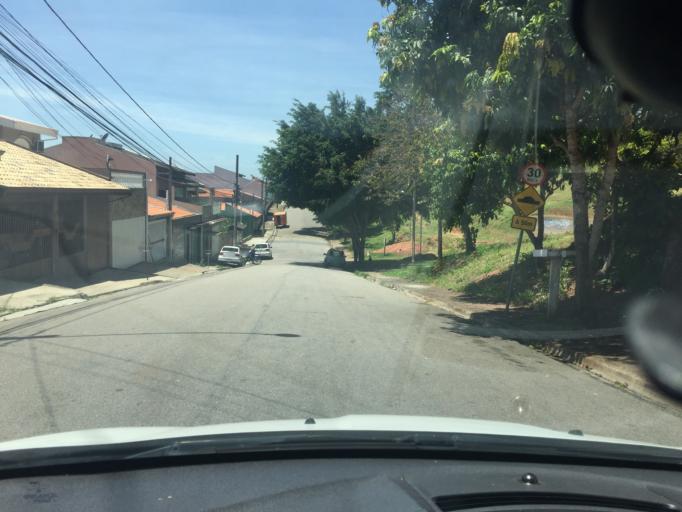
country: BR
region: Sao Paulo
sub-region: Jundiai
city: Jundiai
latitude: -23.2292
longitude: -46.8833
